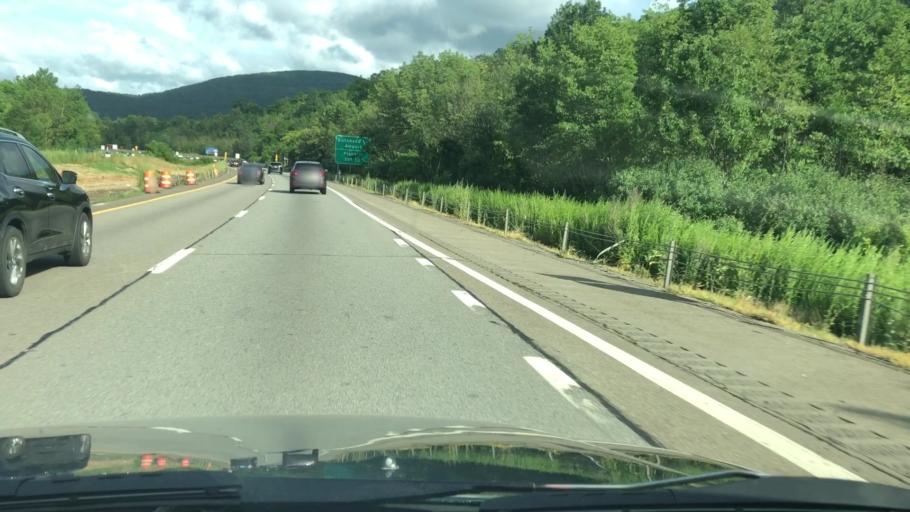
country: US
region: New York
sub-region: Dutchess County
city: Fishkill
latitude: 41.5241
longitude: -73.9107
